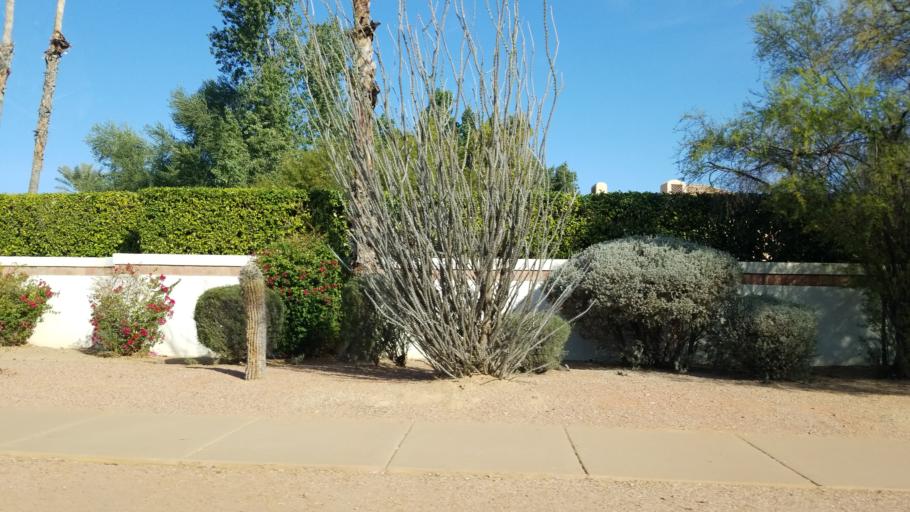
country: US
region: Arizona
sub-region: Maricopa County
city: Paradise Valley
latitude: 33.5676
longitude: -111.9355
